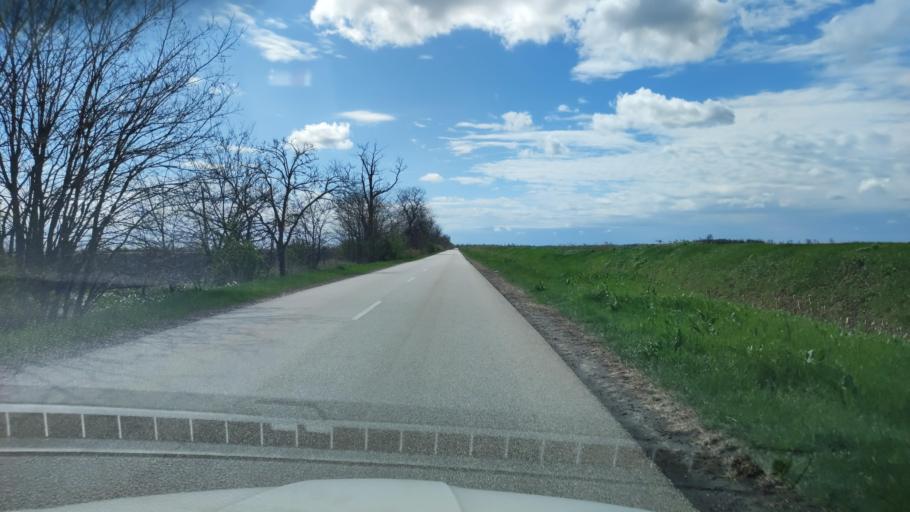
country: HU
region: Pest
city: Abony
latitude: 47.1423
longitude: 20.0109
